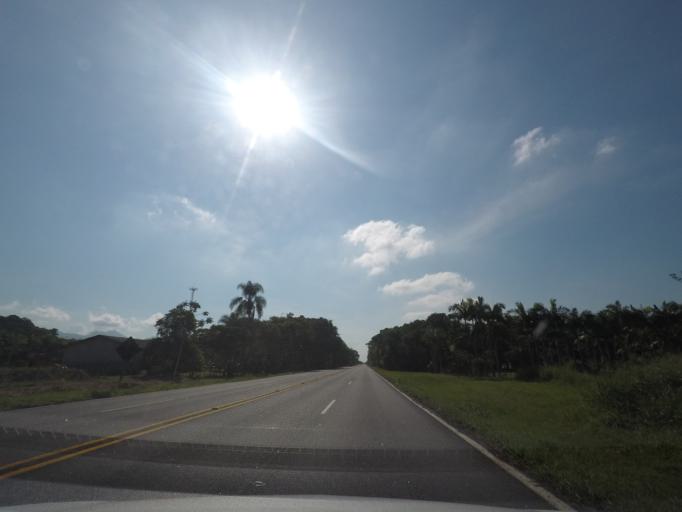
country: BR
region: Parana
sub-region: Pontal Do Parana
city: Pontal do Parana
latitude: -25.6444
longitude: -48.5901
